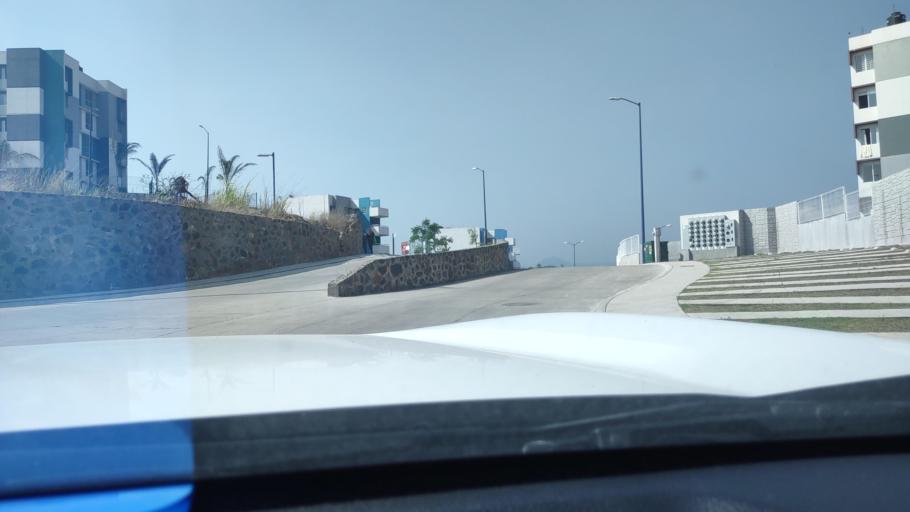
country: MX
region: Veracruz
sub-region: Emiliano Zapata
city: Jacarandas
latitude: 19.5121
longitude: -96.8493
